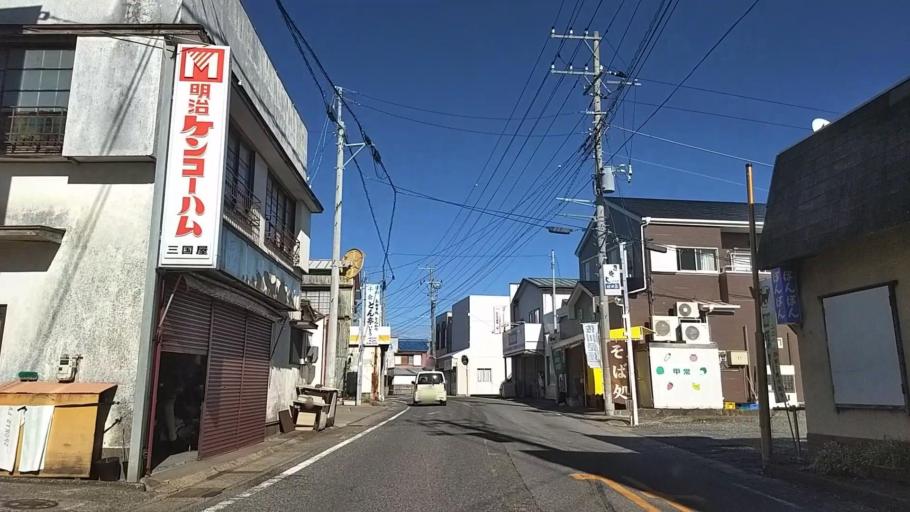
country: JP
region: Chiba
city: Tateyama
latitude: 34.9577
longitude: 139.9593
